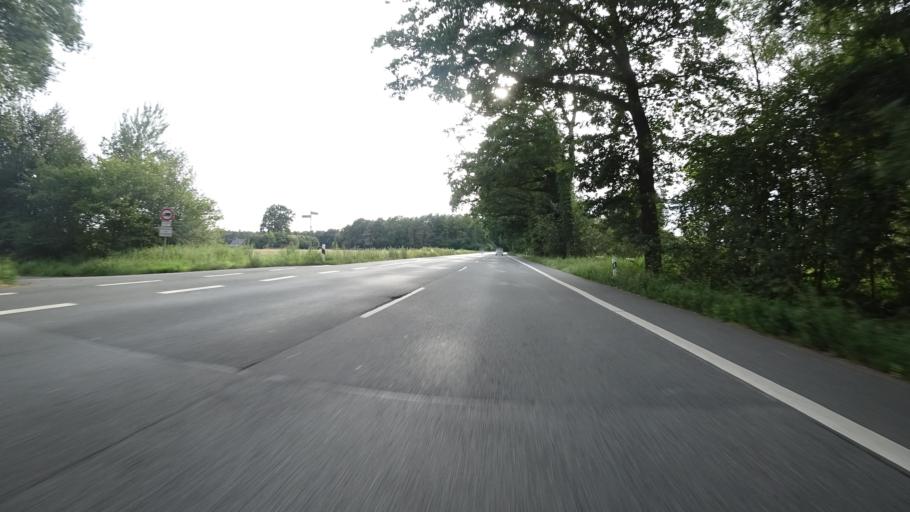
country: DE
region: North Rhine-Westphalia
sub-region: Regierungsbezirk Detmold
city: Harsewinkel
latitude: 51.9413
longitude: 8.2853
